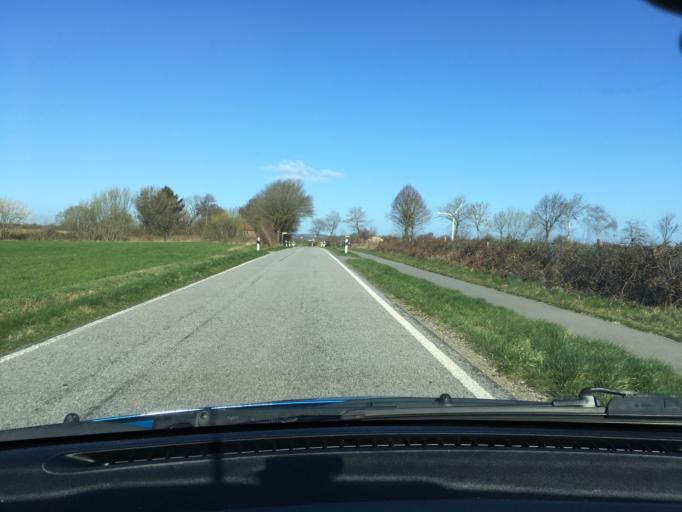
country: DE
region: Schleswig-Holstein
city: Borgwedel
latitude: 54.4976
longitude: 9.6498
